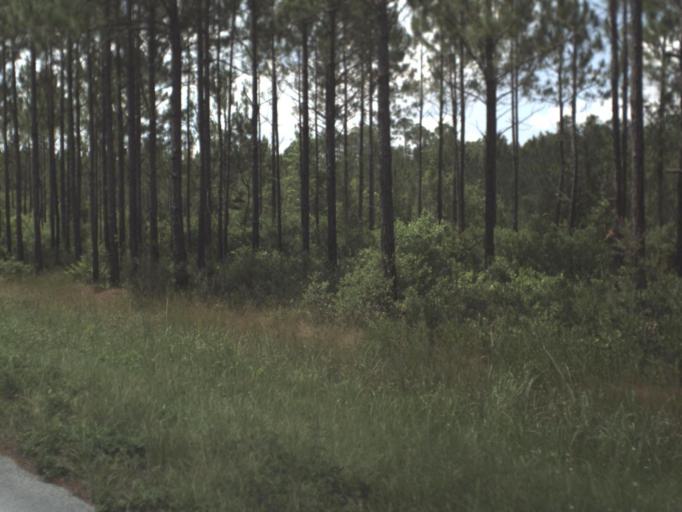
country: US
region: Florida
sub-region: Baker County
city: Macclenny
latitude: 30.5318
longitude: -82.3142
